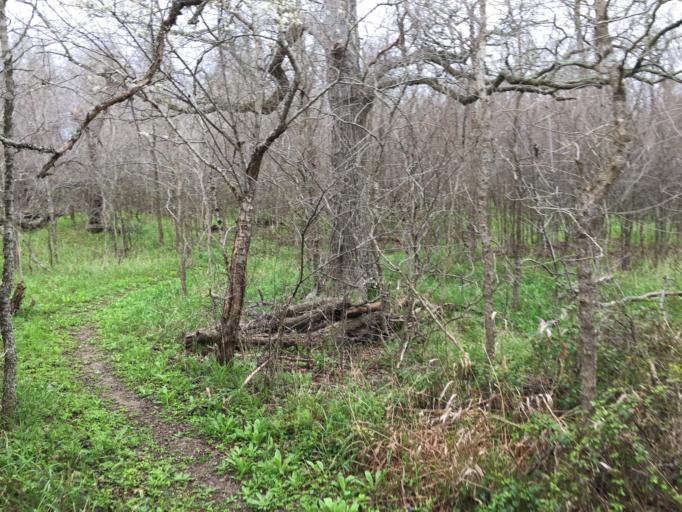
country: US
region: Texas
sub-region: Bastrop County
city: Bastrop
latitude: 30.0883
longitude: -97.3176
